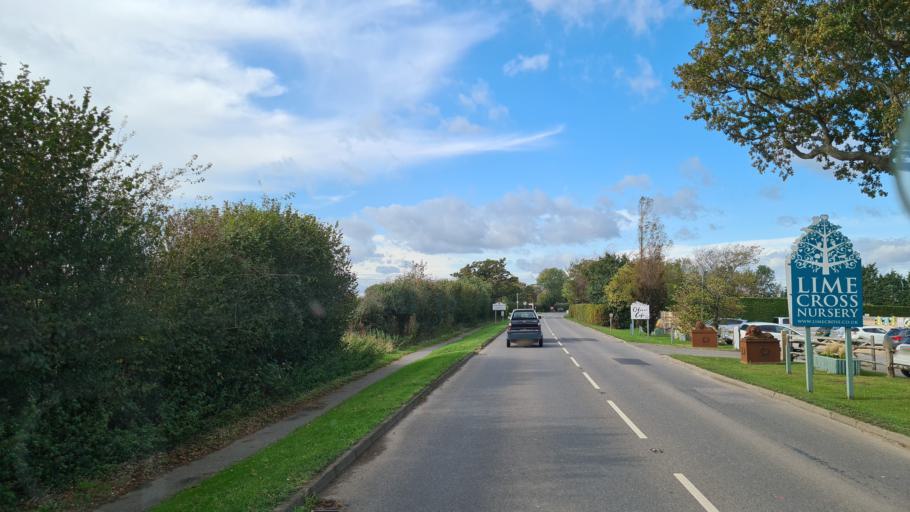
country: GB
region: England
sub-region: East Sussex
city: Bodle Street
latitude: 50.8872
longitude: 0.3326
